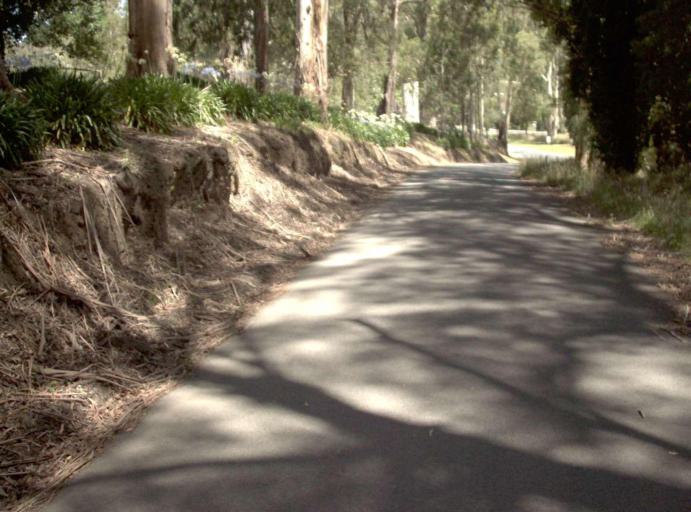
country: AU
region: Victoria
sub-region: Baw Baw
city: Warragul
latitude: -37.8895
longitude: 145.9987
